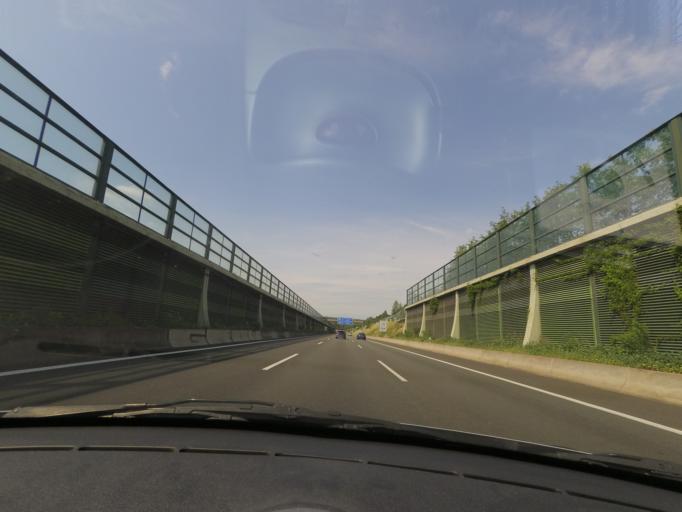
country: DE
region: Saxony
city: Wittgensdorf
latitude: 50.8692
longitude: 12.8897
